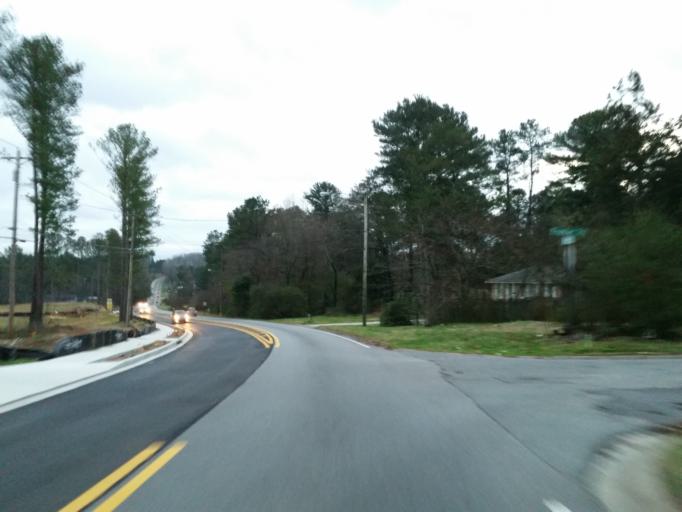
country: US
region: Georgia
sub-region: Cobb County
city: Fair Oaks
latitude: 33.8746
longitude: -84.5798
